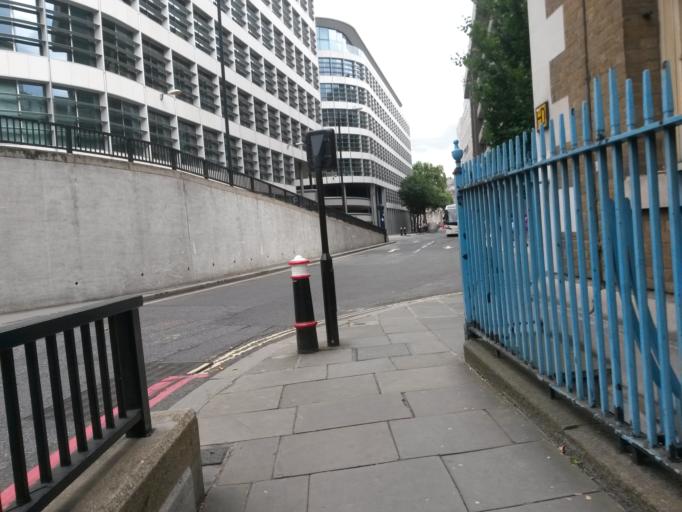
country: GB
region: England
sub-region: Greater London
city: City of London
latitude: 51.5090
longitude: -0.0813
